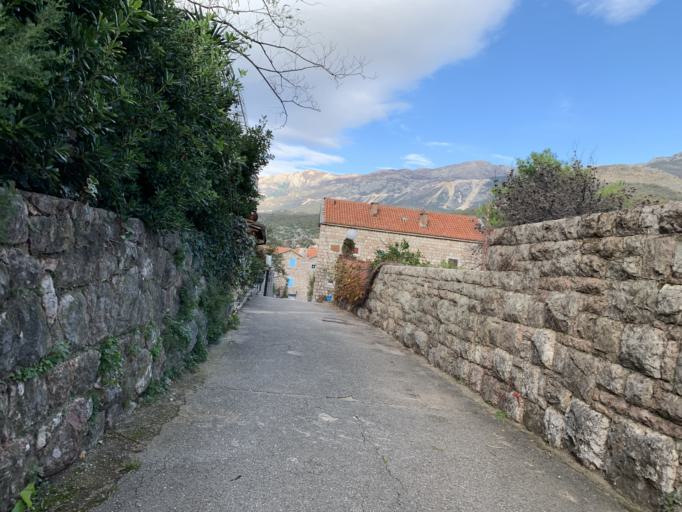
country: ME
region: Budva
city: Budva
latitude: 42.2666
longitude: 18.8918
